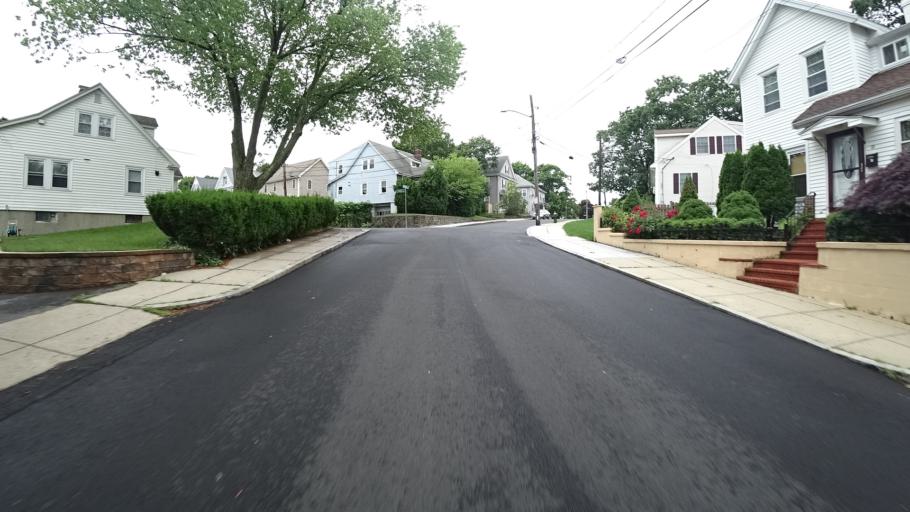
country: US
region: Massachusetts
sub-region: Norfolk County
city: Dedham
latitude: 42.2419
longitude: -71.1431
